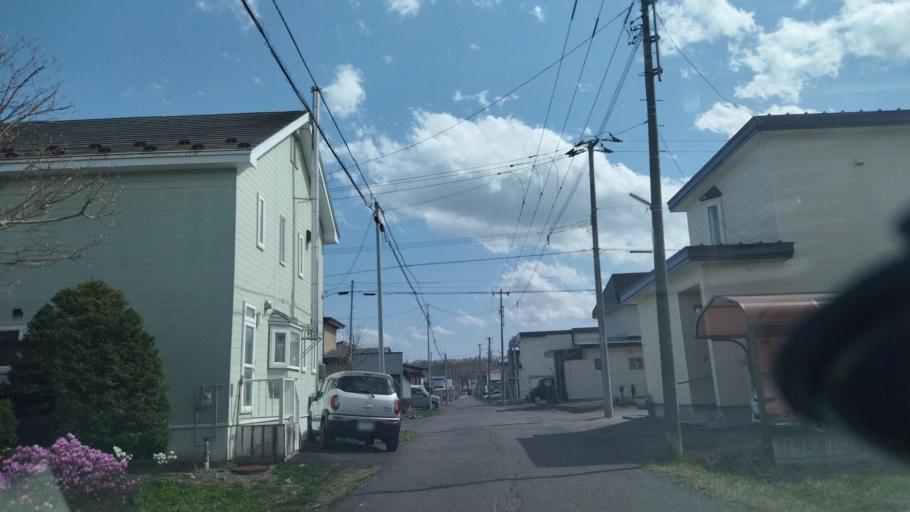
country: JP
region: Hokkaido
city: Obihiro
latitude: 42.9076
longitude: 143.1588
